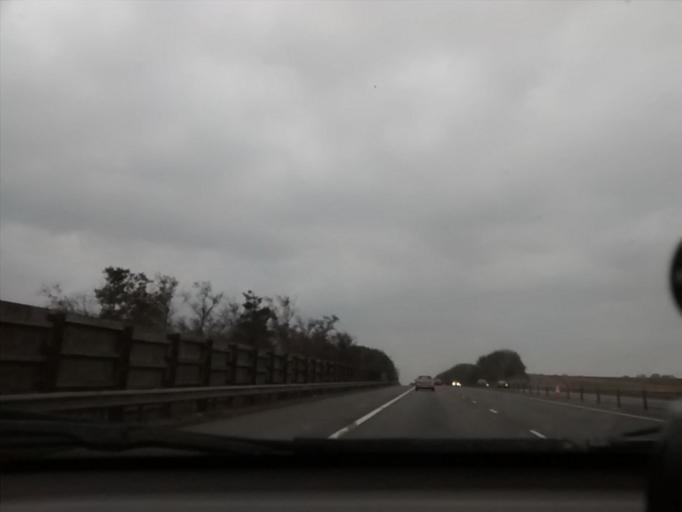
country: GB
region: England
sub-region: Essex
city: Saffron Walden
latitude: 51.9980
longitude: 0.1949
